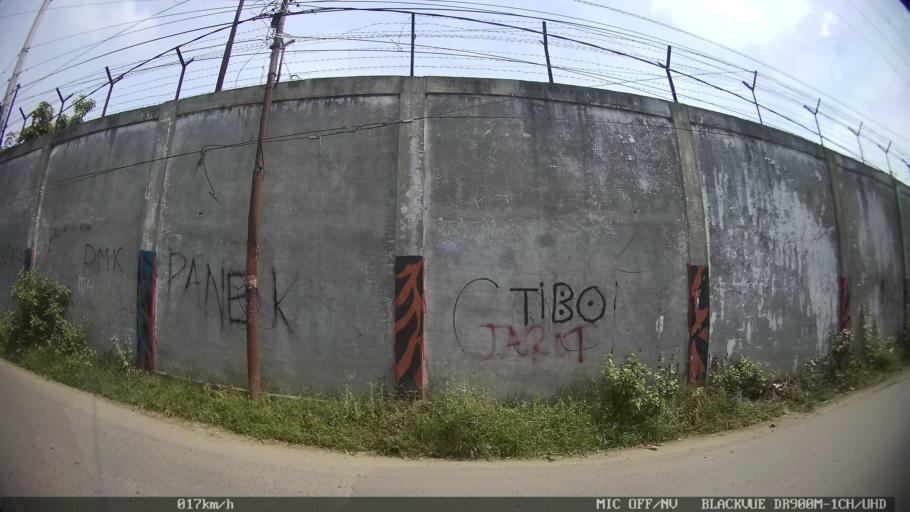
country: ID
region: North Sumatra
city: Medan
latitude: 3.6505
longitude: 98.7168
